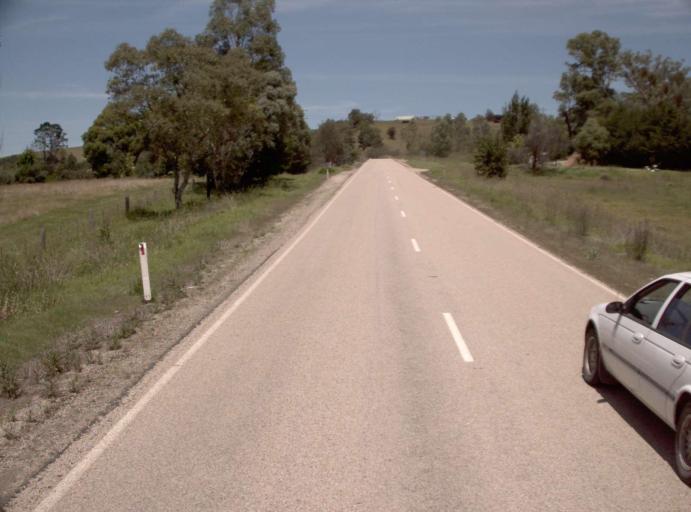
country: AU
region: Victoria
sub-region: East Gippsland
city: Bairnsdale
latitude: -37.5027
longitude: 147.8411
